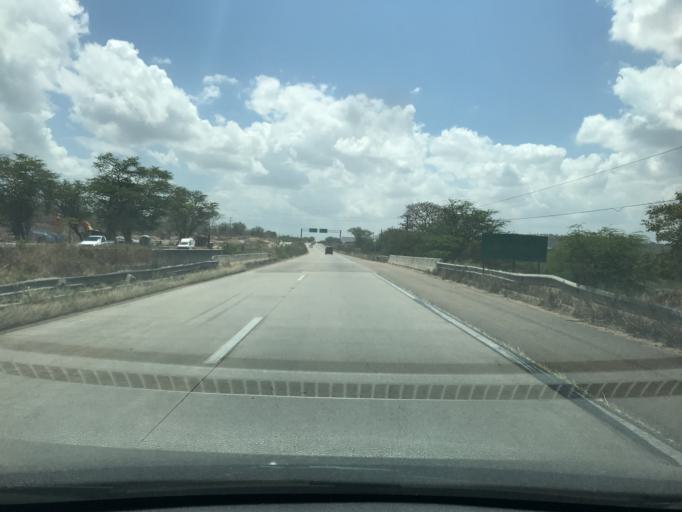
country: BR
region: Pernambuco
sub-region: Bezerros
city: Bezerros
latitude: -8.2984
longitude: -35.8583
